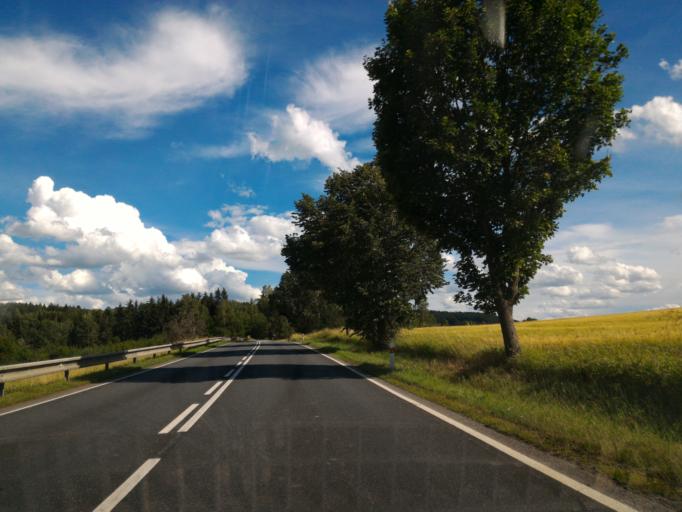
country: CZ
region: Vysocina
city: Dolni Cerekev
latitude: 49.3385
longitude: 15.4866
